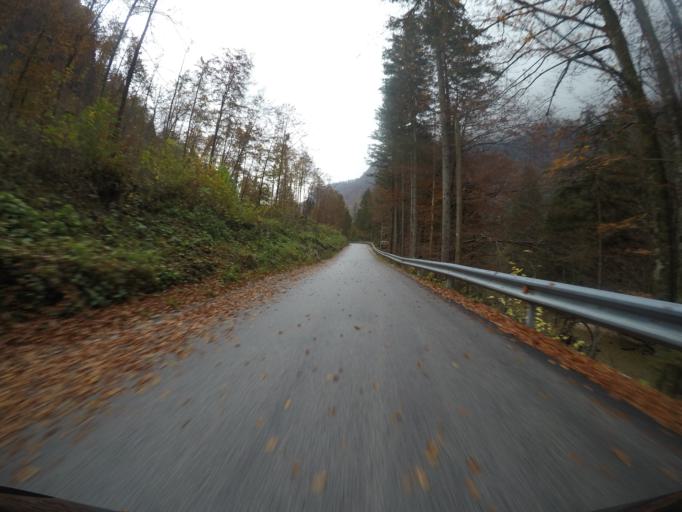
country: SI
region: Jesenice
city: Hrusica
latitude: 46.3977
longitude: 14.0016
